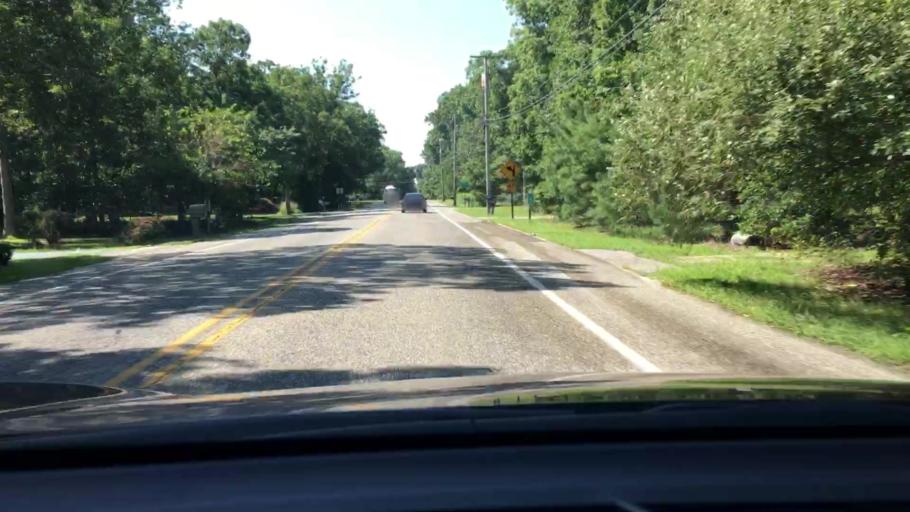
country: US
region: New Jersey
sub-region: Cape May County
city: Woodbine
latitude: 39.2611
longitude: -74.8047
